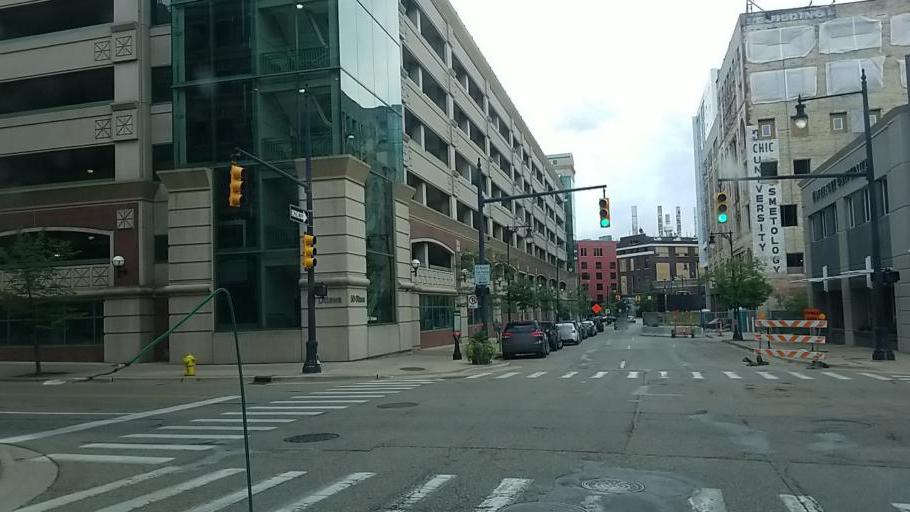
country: US
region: Michigan
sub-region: Kent County
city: Grand Rapids
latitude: 42.9644
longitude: -85.6709
